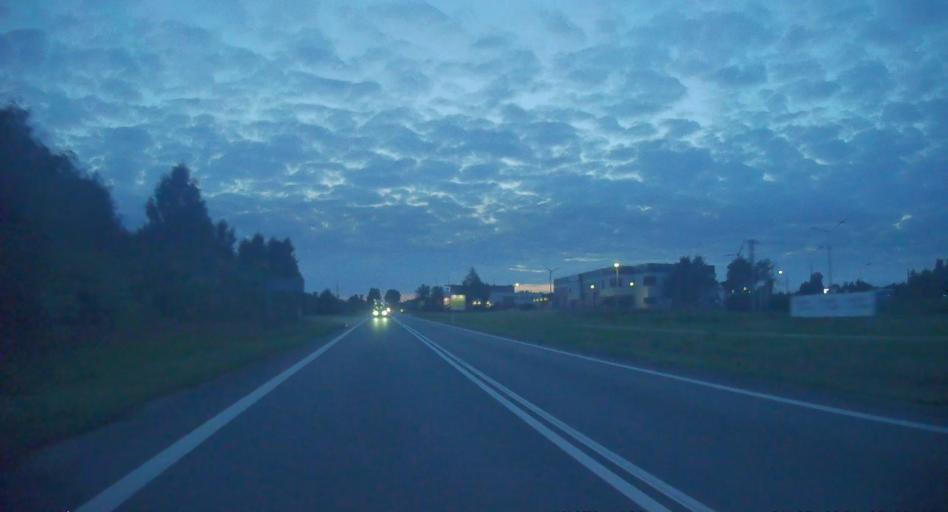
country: PL
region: Silesian Voivodeship
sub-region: Powiat klobucki
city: Klobuck
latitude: 50.9060
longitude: 18.9212
